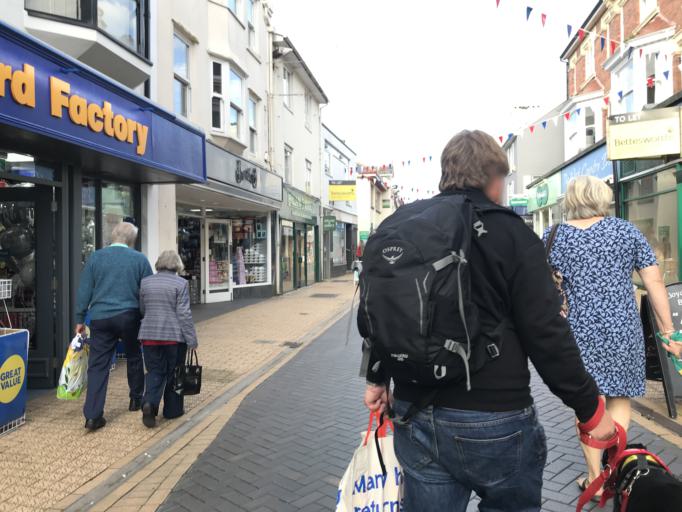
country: GB
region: England
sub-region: Borough of Torbay
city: Brixham
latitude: 50.3948
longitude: -3.5142
